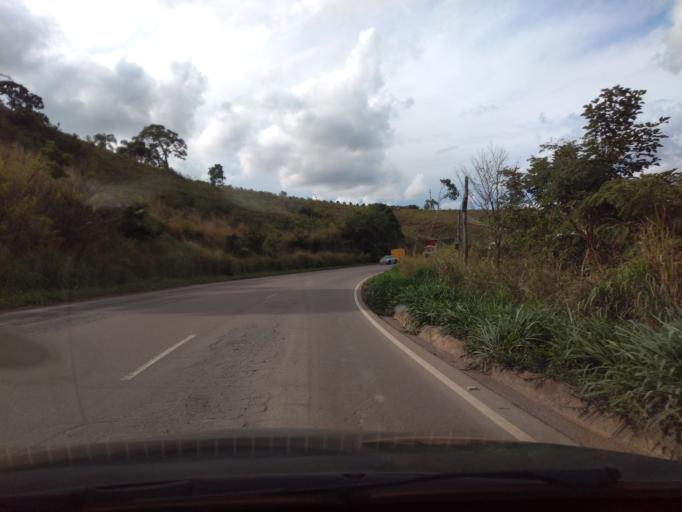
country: BR
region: Minas Gerais
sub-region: Varginha
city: Varginha
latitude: -21.6091
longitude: -45.4329
